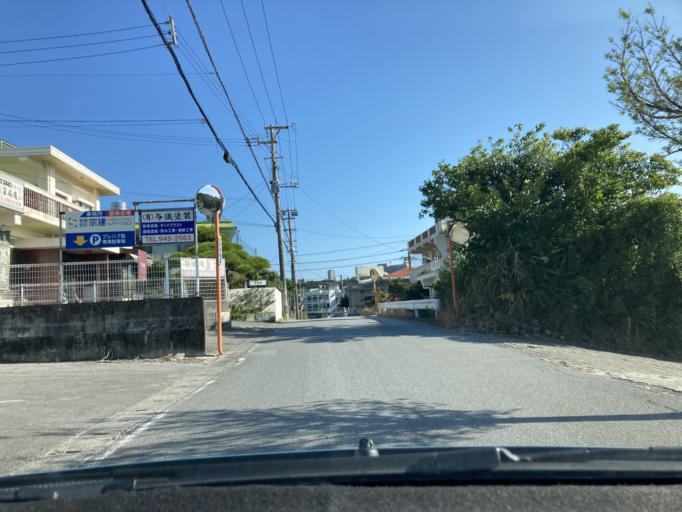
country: JP
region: Okinawa
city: Ginowan
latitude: 26.2512
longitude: 127.7541
